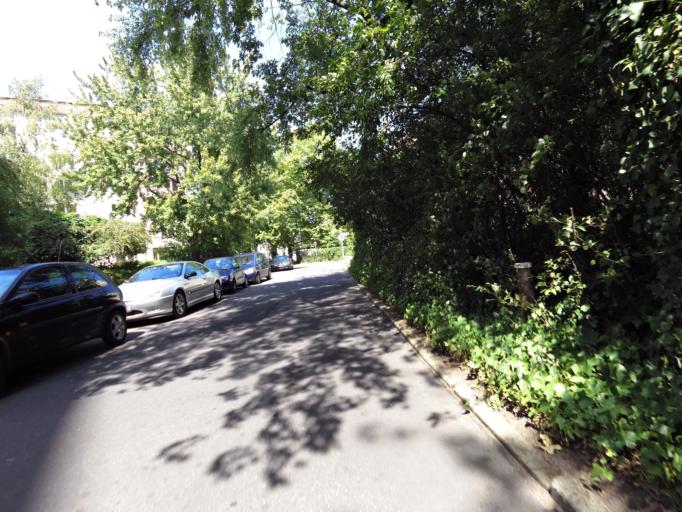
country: DE
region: Berlin
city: Lankwitz
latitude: 52.4317
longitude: 13.3422
